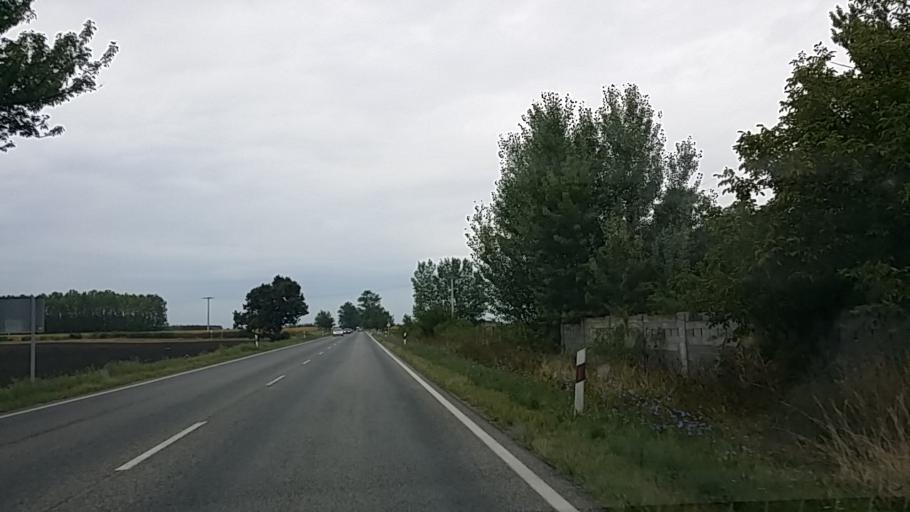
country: HU
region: Gyor-Moson-Sopron
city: Kapuvar
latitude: 47.5885
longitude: 17.0847
